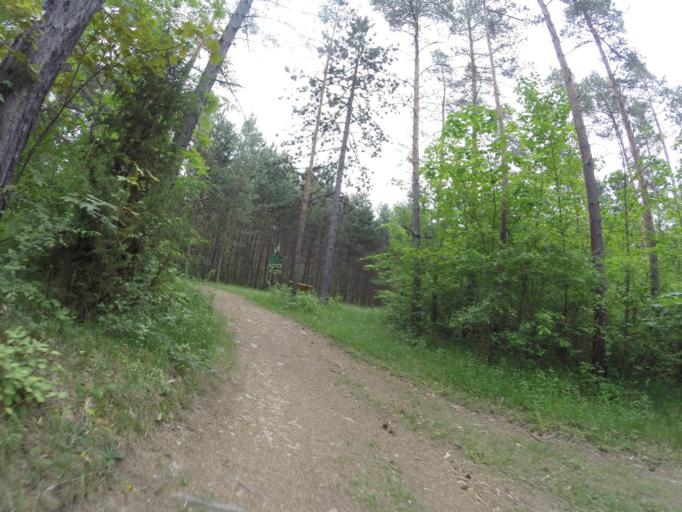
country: DE
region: Thuringia
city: Sulza
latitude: 50.9000
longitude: 11.6169
